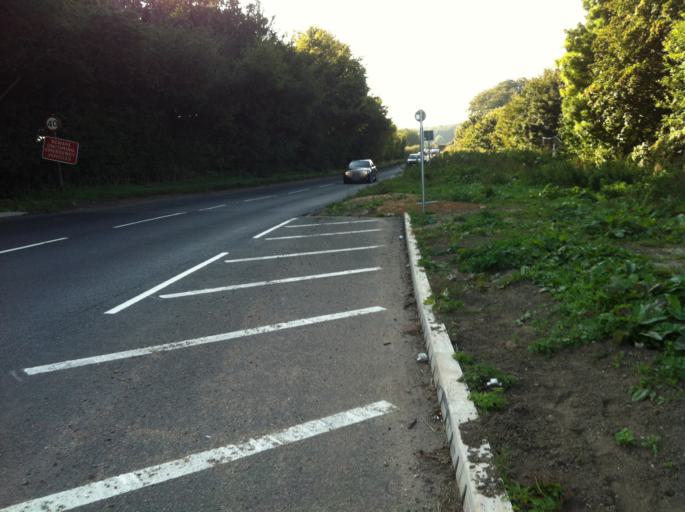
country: GB
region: England
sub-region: Norfolk
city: Bowthorpe
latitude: 52.6241
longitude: 1.2135
